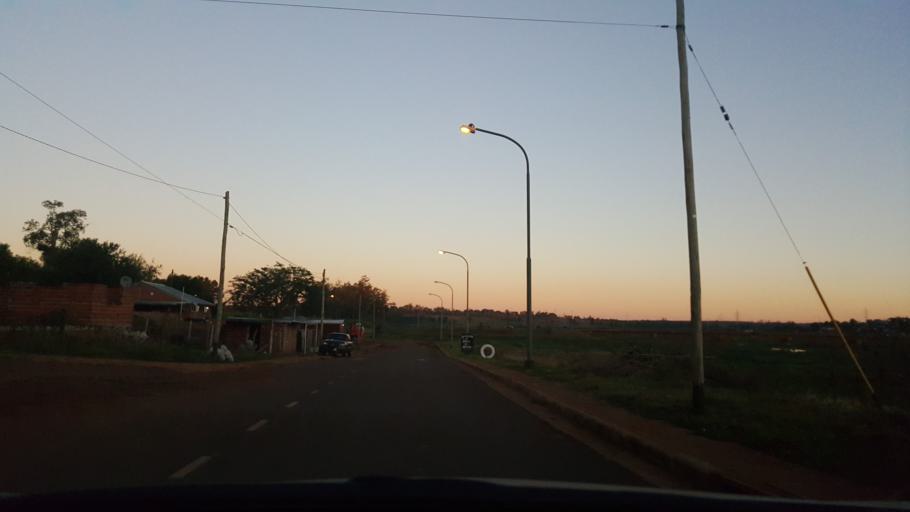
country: AR
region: Misiones
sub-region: Departamento de Capital
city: Posadas
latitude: -27.4254
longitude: -55.9033
